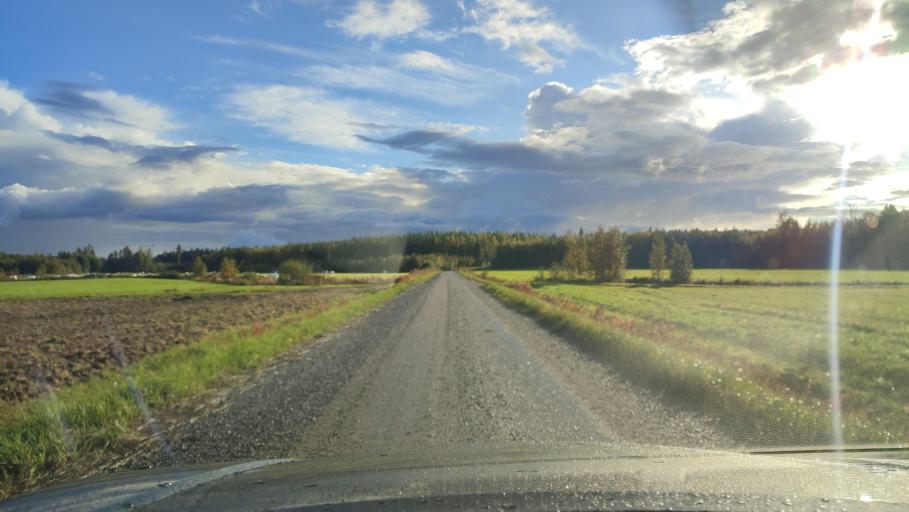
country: FI
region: Southern Ostrobothnia
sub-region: Suupohja
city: Karijoki
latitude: 62.3111
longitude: 21.5489
